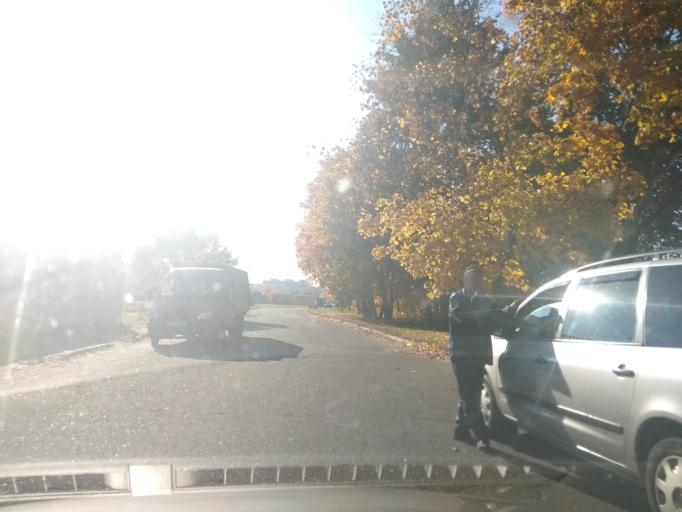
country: BY
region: Grodnenskaya
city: Vawkavysk
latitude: 53.1559
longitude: 24.4737
